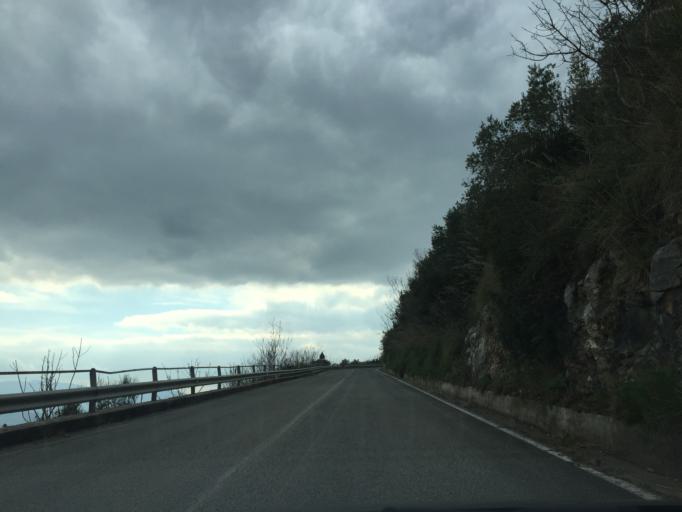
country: IT
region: Latium
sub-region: Provincia di Frosinone
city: Cassino
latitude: 41.4873
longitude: 13.8185
